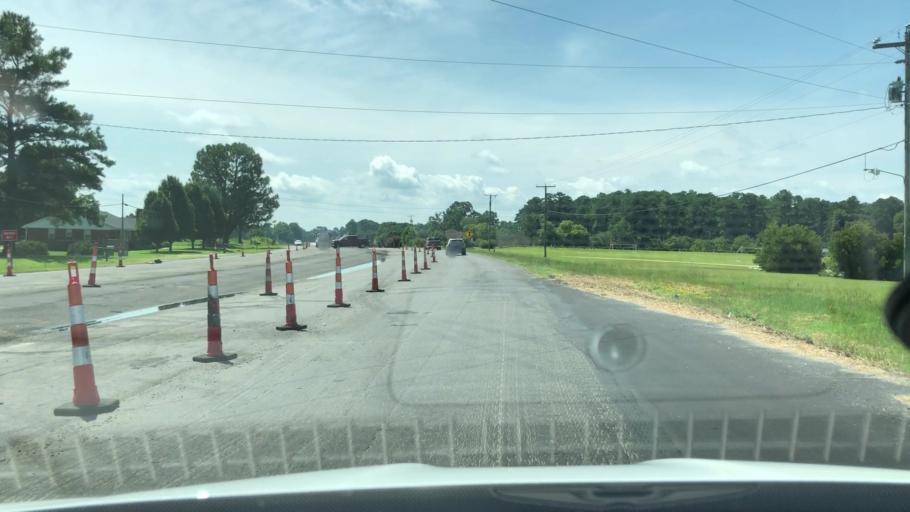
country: US
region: North Carolina
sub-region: Martin County
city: Williamston
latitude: 35.8151
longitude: -77.0649
